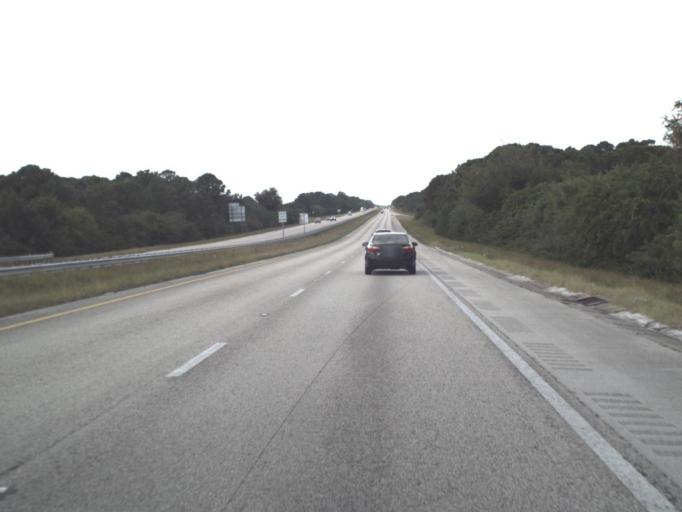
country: US
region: Florida
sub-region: Brevard County
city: Cocoa
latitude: 28.4017
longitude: -80.7656
